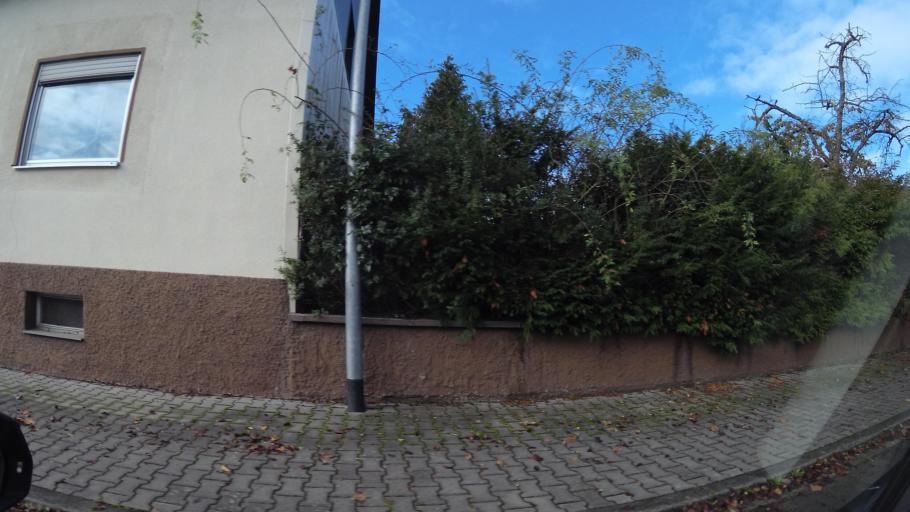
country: DE
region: Rheinland-Pfalz
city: Ramstein-Miesenbach
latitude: 49.4423
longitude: 7.5522
